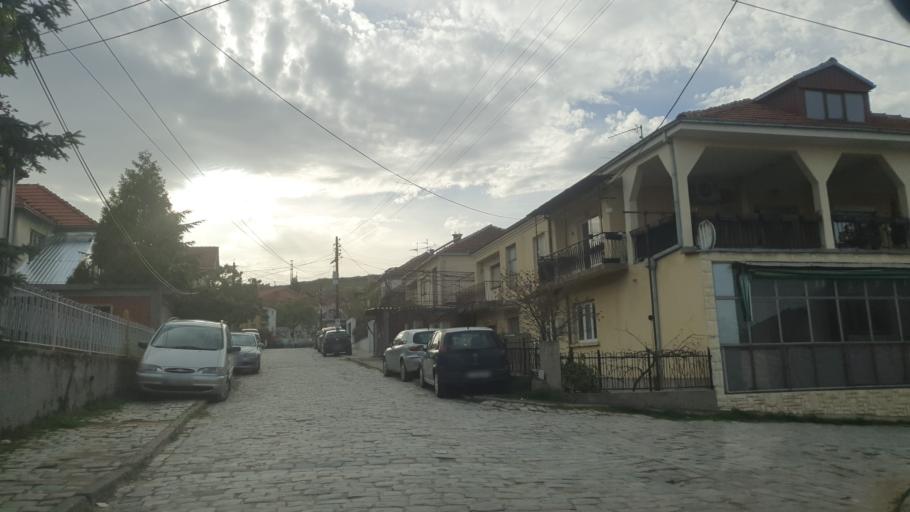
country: MK
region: Bitola
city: Bitola
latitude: 41.0354
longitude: 21.3263
